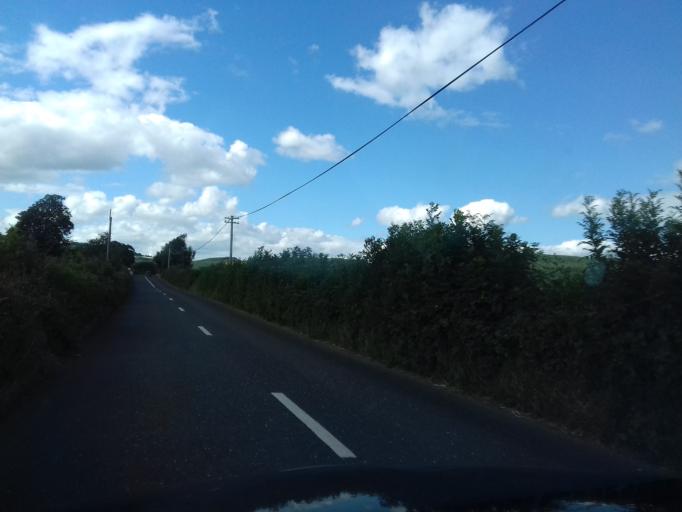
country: IE
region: Munster
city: Carrick-on-Suir
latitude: 52.3810
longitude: -7.4572
